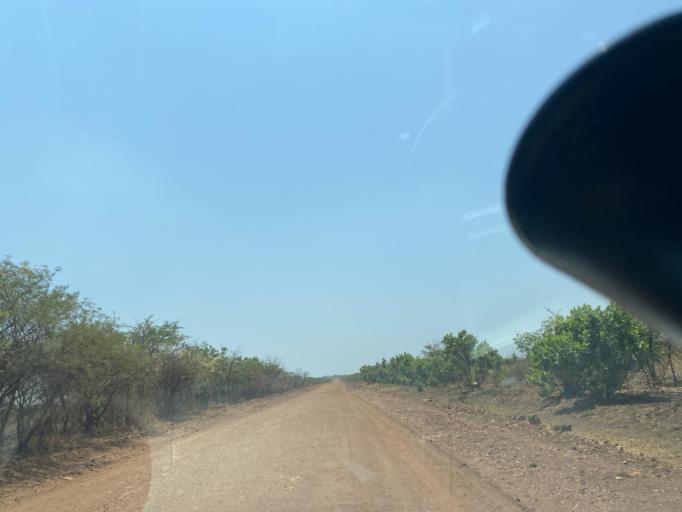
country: ZM
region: Lusaka
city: Lusaka
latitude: -15.4573
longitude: 27.9362
